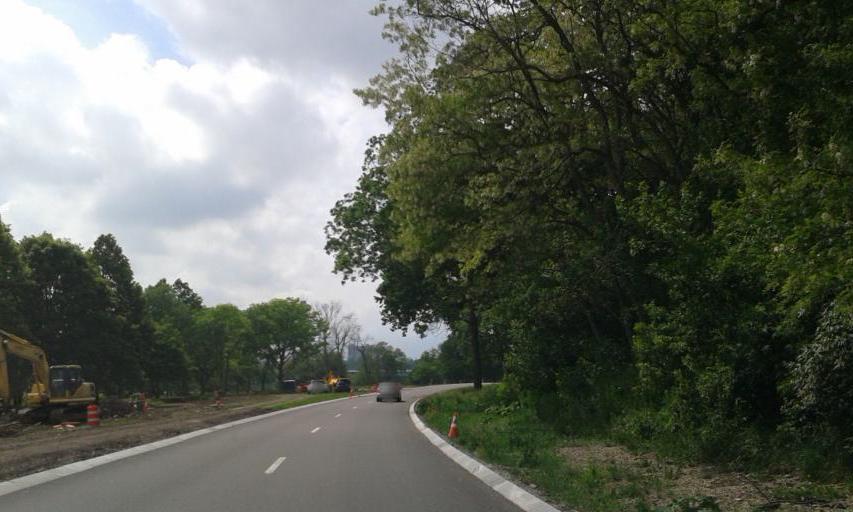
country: US
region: New York
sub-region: Niagara County
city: Niagara Falls
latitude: 43.0811
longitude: -79.0589
